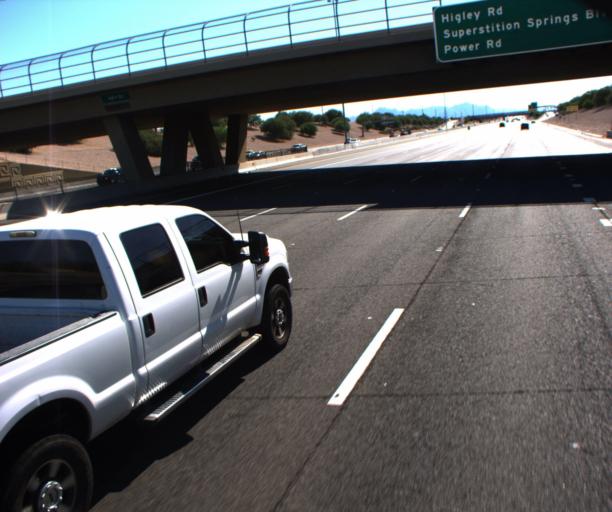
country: US
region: Arizona
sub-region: Maricopa County
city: Gilbert
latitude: 33.3863
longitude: -111.7285
